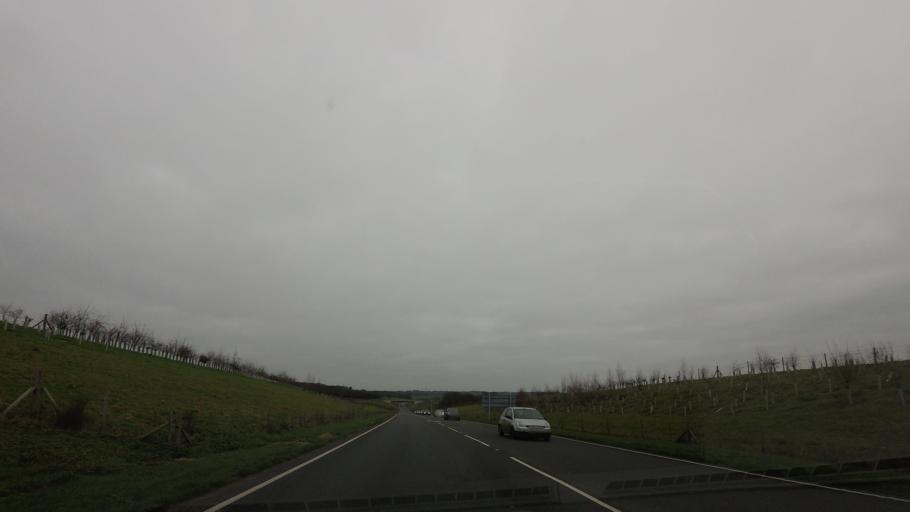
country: GB
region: England
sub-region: East Sussex
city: Bexhill-on-Sea
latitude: 50.8593
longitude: 0.4812
